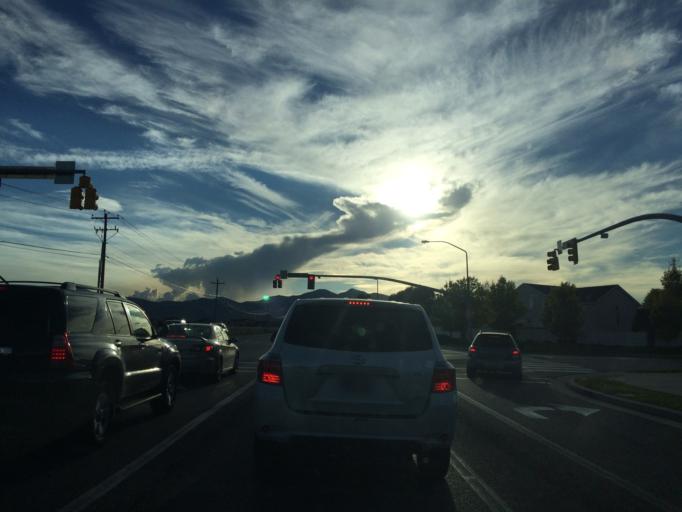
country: US
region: Utah
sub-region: Salt Lake County
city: Oquirrh
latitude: 40.6094
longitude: -112.0050
